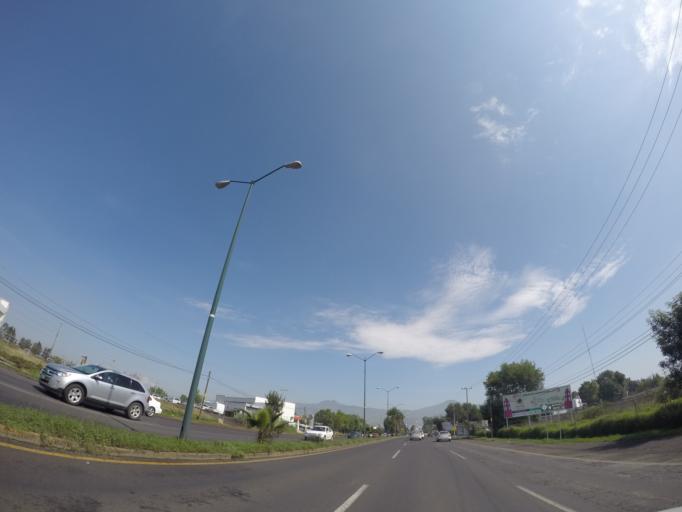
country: MX
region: Michoacan
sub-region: Morelia
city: Morelos
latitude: 19.6794
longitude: -101.2346
